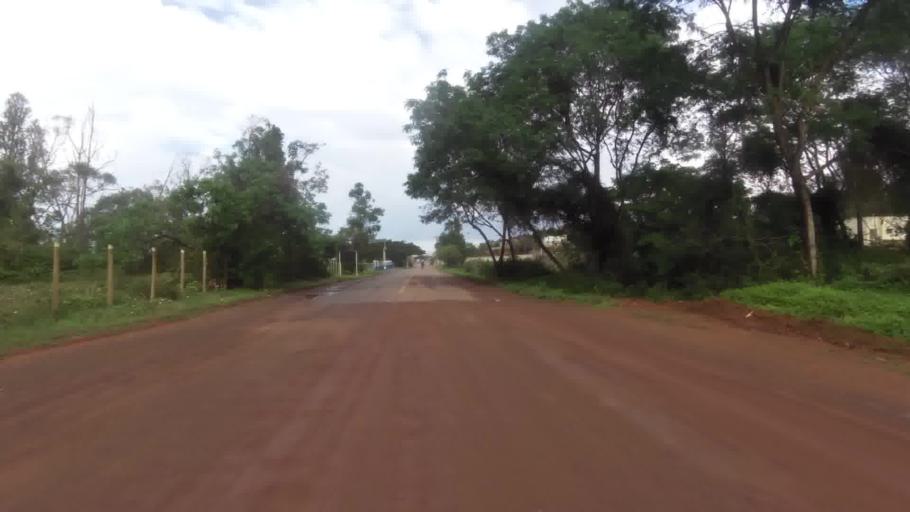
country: BR
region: Espirito Santo
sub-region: Piuma
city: Piuma
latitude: -20.7956
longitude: -40.6385
